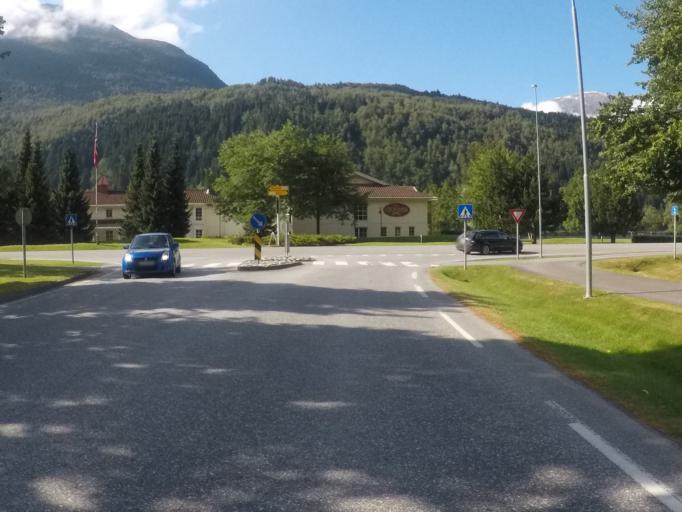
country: NO
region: Sogn og Fjordane
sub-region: Stryn
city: Stryn
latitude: 61.8718
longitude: 6.8461
